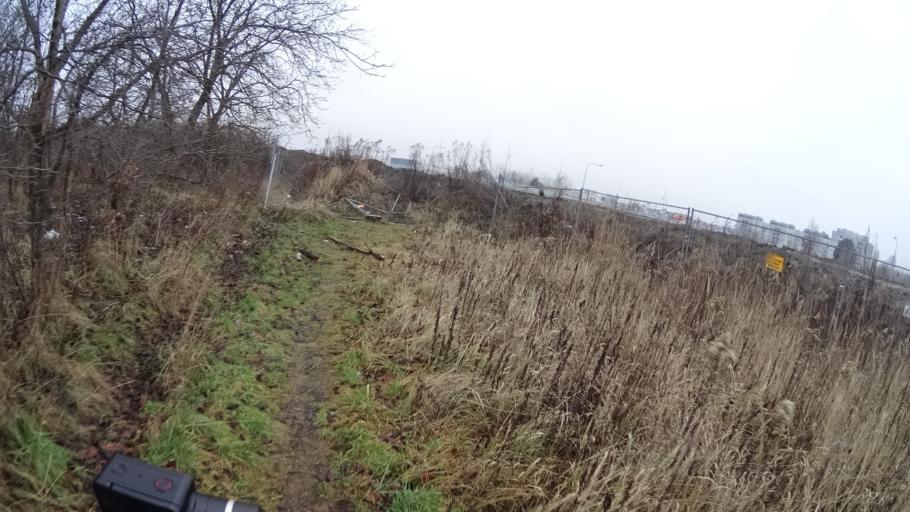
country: PL
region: Masovian Voivodeship
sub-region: Warszawa
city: Ursynow
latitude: 52.1397
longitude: 21.0318
